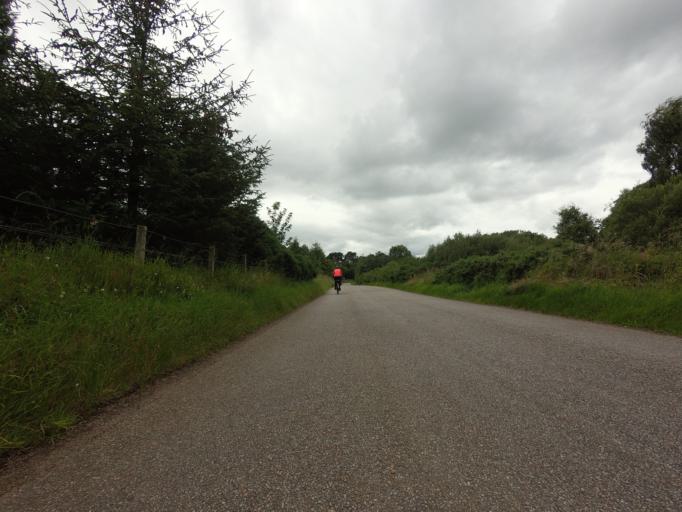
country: GB
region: Scotland
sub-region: Highland
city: Nairn
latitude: 57.5978
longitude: -3.8040
